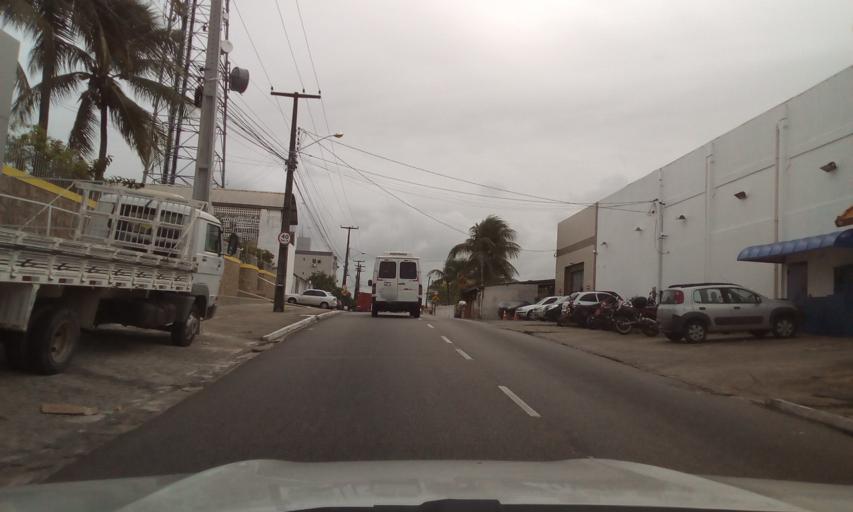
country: BR
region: Paraiba
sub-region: Joao Pessoa
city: Joao Pessoa
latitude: -7.1013
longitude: -34.8636
